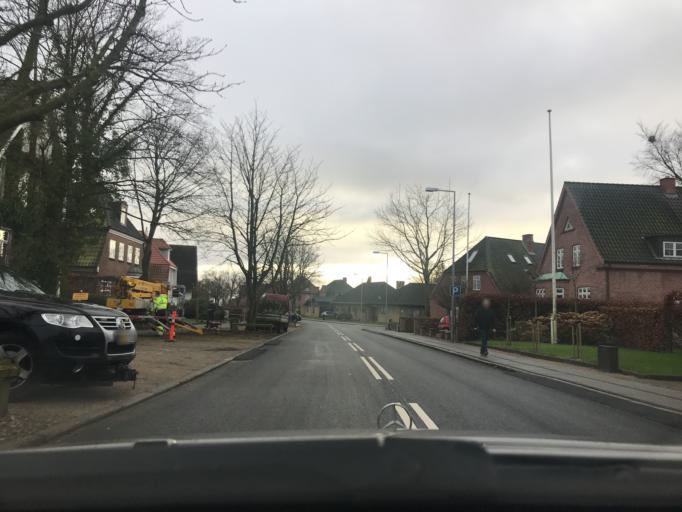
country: DK
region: South Denmark
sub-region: Sonderborg Kommune
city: Sonderborg
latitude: 54.9074
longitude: 9.7926
